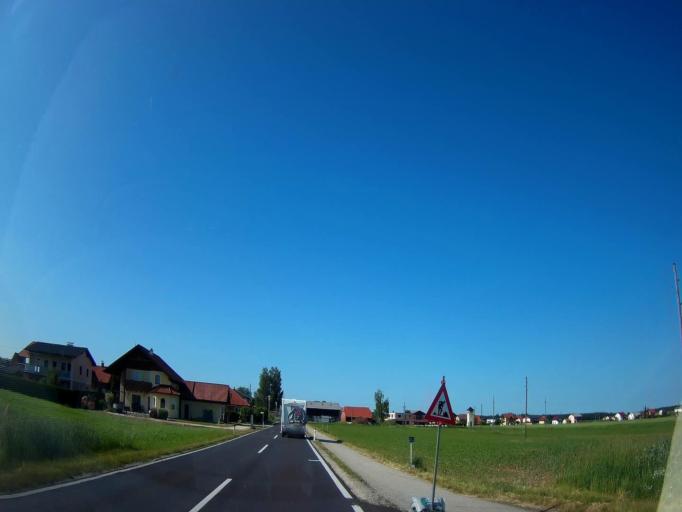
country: AT
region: Upper Austria
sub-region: Politischer Bezirk Braunau am Inn
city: Braunau am Inn
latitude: 48.1739
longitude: 13.0497
